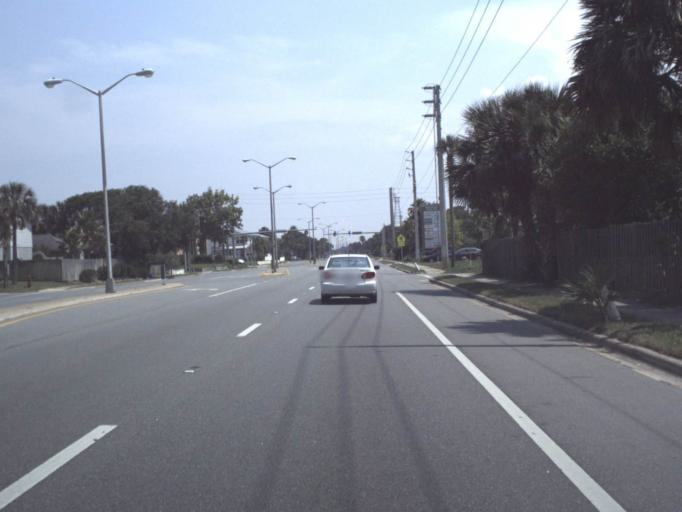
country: US
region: Florida
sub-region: Duval County
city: Neptune Beach
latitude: 30.3164
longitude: -81.3972
